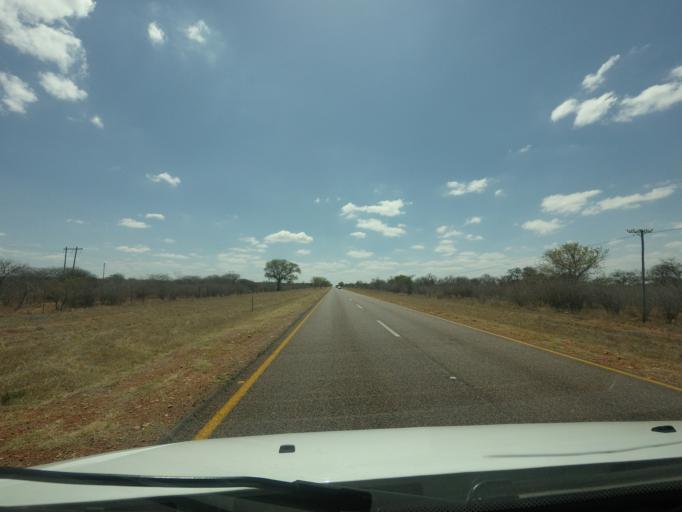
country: ZA
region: Limpopo
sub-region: Capricorn District Municipality
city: Dendron
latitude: -23.5932
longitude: 28.7899
